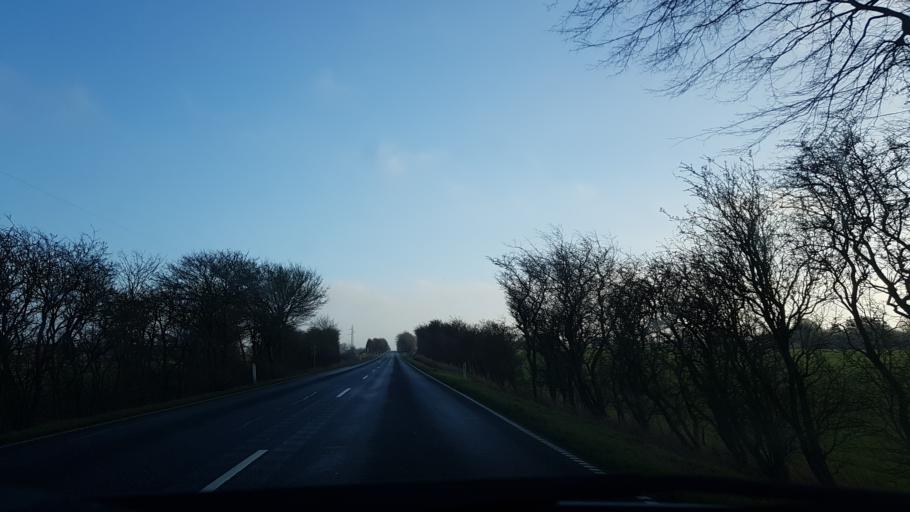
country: DK
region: South Denmark
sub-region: Haderslev Kommune
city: Vojens
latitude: 55.1912
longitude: 9.2124
